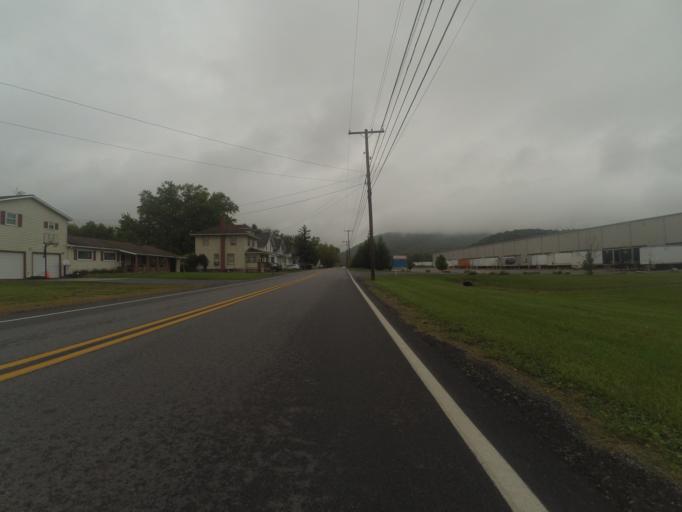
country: US
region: Pennsylvania
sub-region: Huntingdon County
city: McConnellstown
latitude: 40.5625
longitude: -78.1109
